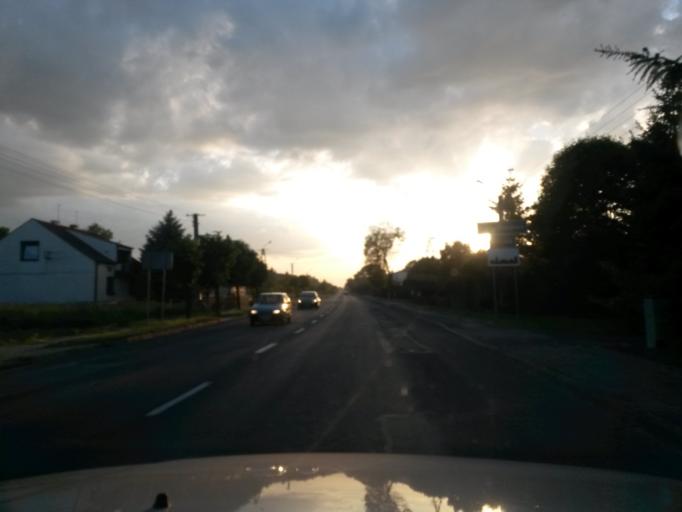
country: PL
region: Lodz Voivodeship
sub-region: Powiat wielunski
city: Mokrsko
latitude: 51.2609
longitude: 18.4782
